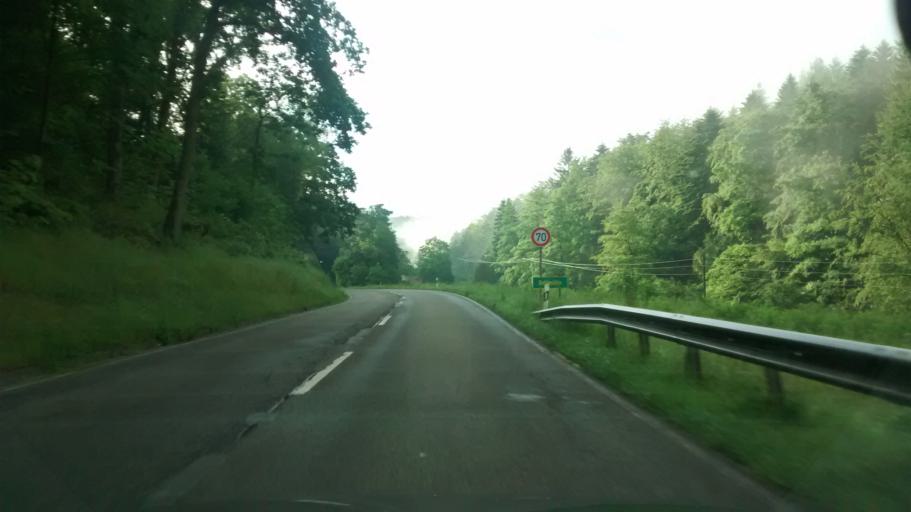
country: DE
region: Rheinland-Pfalz
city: Dorrenbach
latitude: 49.1110
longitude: 7.9562
